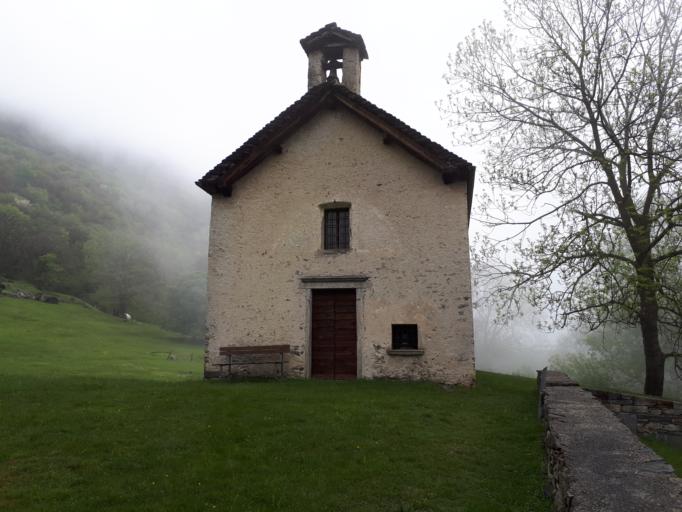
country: CH
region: Ticino
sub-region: Bellinzona District
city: Sementina
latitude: 46.1840
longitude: 8.9654
